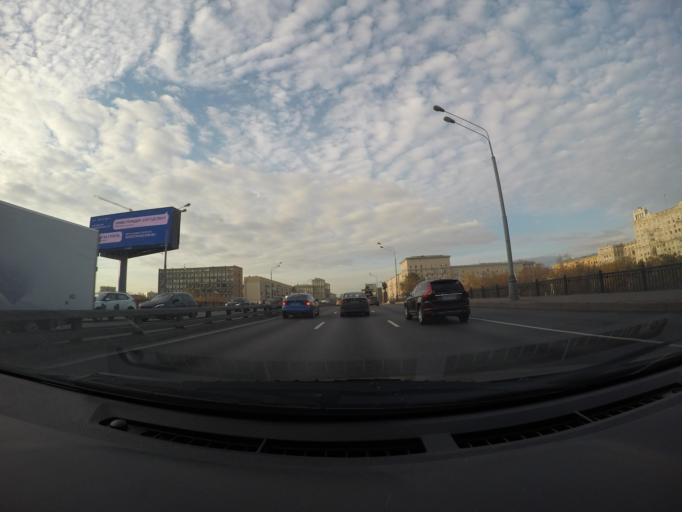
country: RU
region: Moskovskaya
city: Koptevo
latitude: 55.8144
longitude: 37.5017
